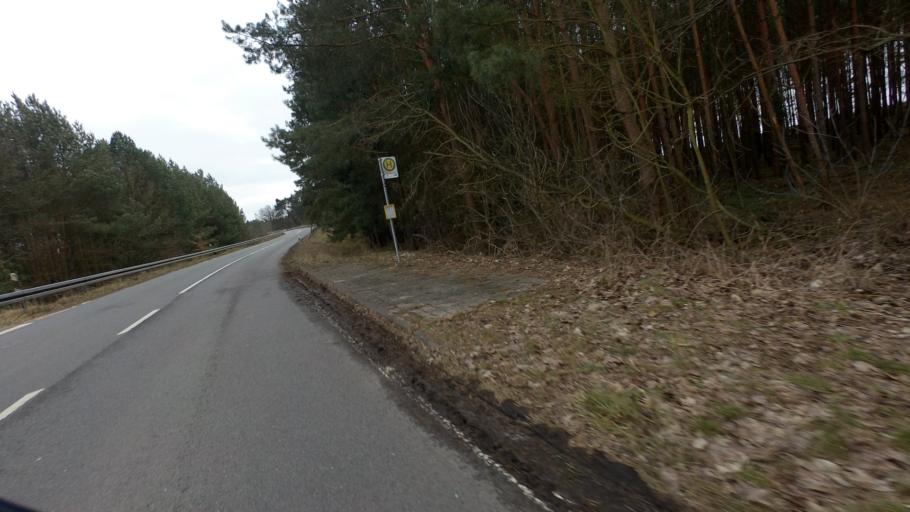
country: DE
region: Brandenburg
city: Trebbin
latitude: 52.1958
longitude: 13.2218
